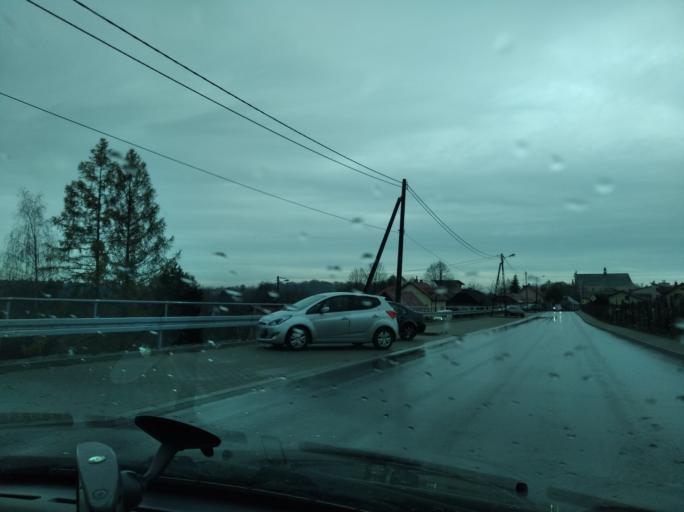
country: PL
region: Subcarpathian Voivodeship
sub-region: Powiat rzeszowski
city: Tyczyn
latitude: 49.9581
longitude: 22.0362
